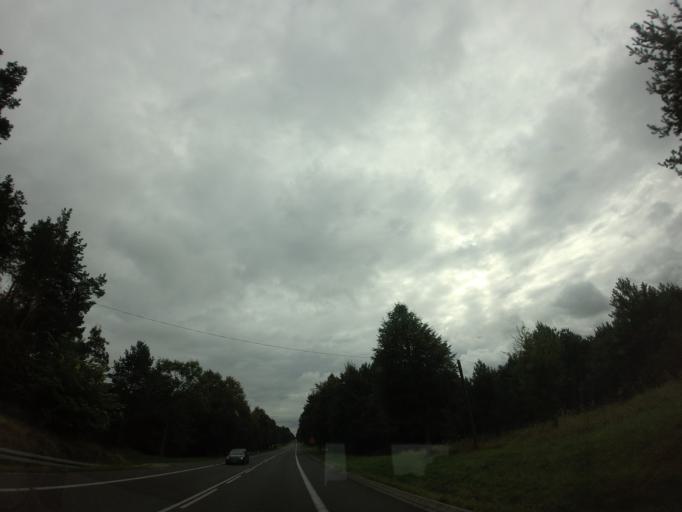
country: PL
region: West Pomeranian Voivodeship
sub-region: Powiat goleniowski
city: Przybiernow
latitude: 53.7425
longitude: 14.7756
